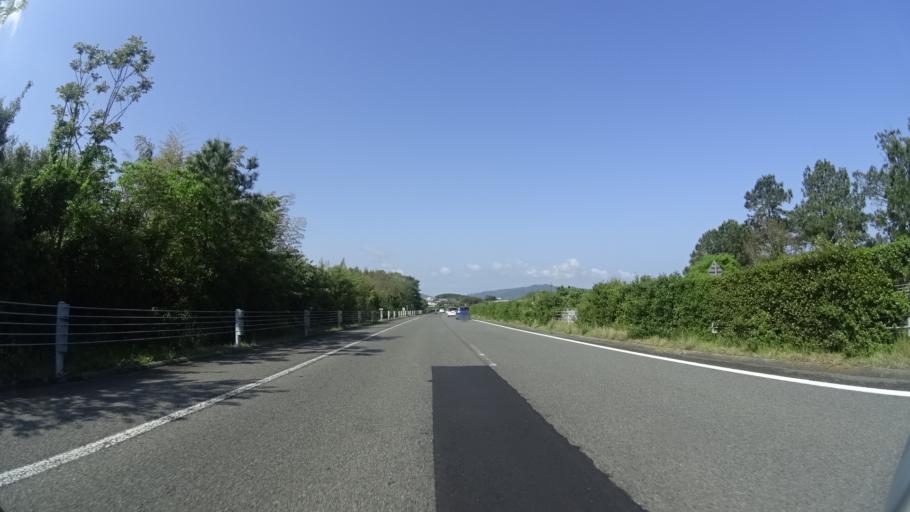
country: JP
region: Hyogo
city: Fukura
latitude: 34.3269
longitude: 134.7898
